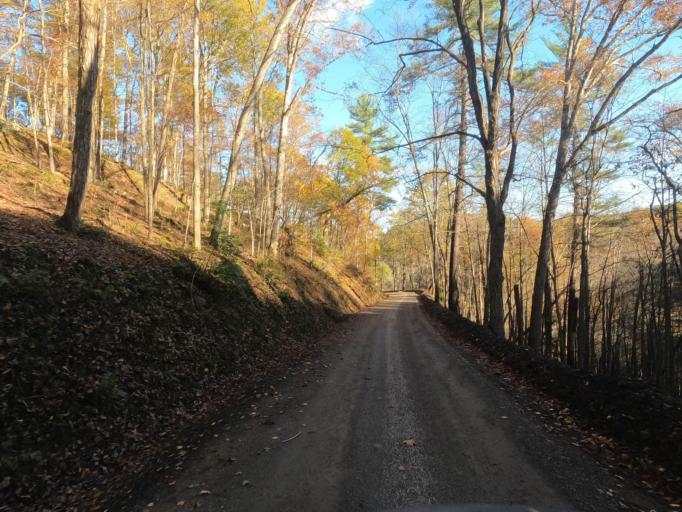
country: US
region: West Virginia
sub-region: Morgan County
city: Berkeley Springs
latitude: 39.6587
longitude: -78.4585
